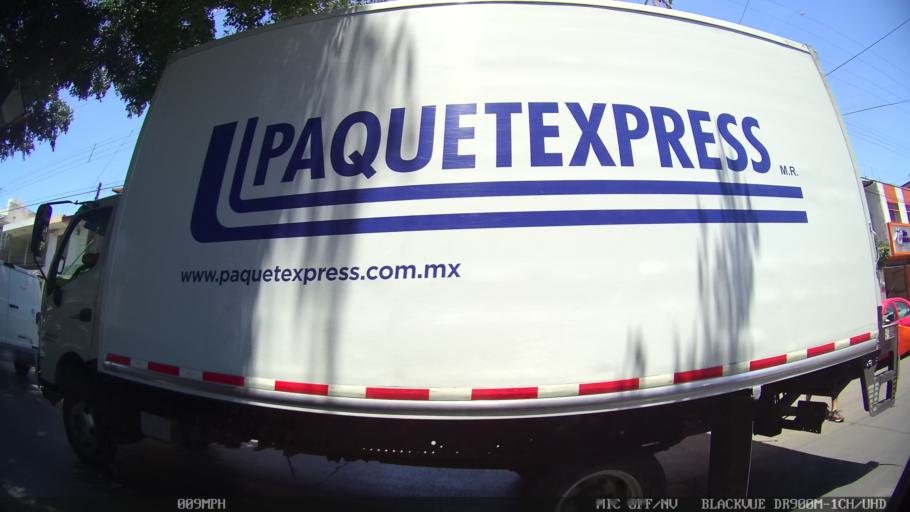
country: MX
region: Jalisco
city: Tlaquepaque
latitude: 20.6661
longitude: -103.2761
